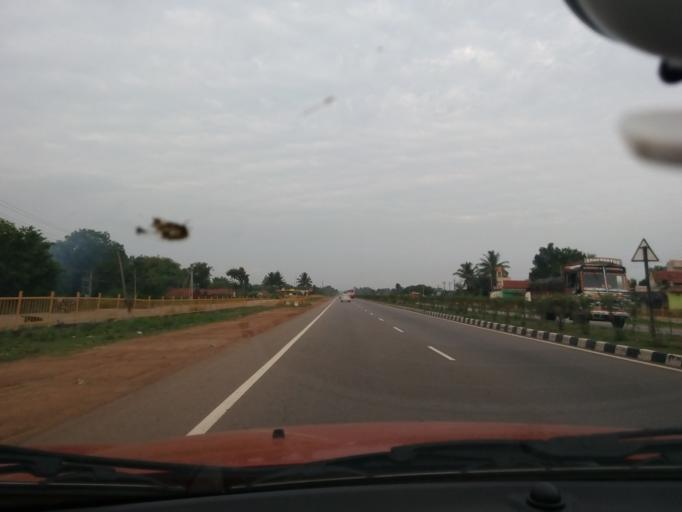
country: IN
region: Karnataka
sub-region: Tumkur
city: Kunigal
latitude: 12.9932
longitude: 76.8946
